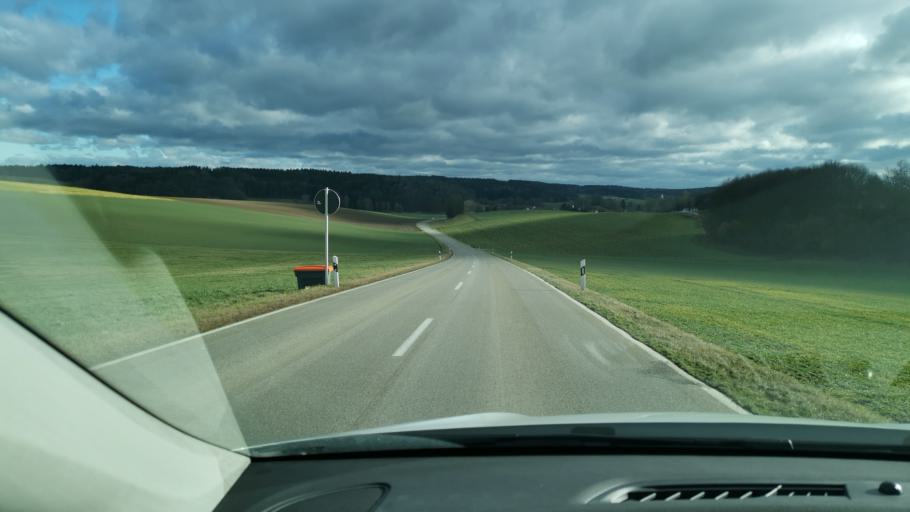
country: DE
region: Bavaria
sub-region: Swabia
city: Aindling
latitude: 48.5588
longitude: 10.9711
